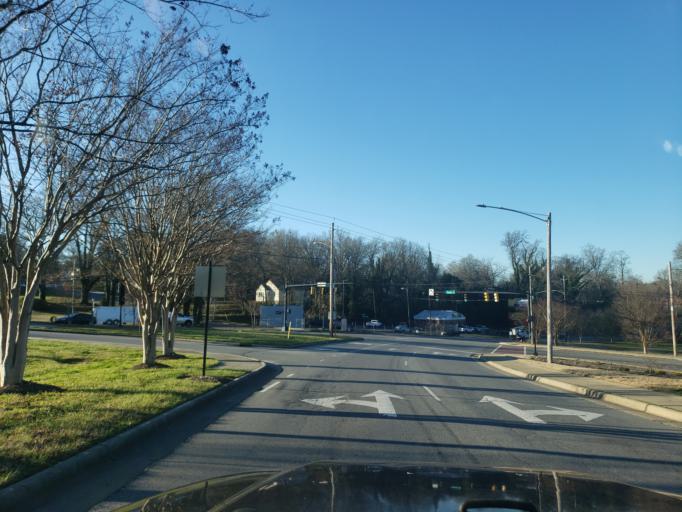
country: US
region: North Carolina
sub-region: Gaston County
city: Gastonia
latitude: 35.2670
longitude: -81.1870
